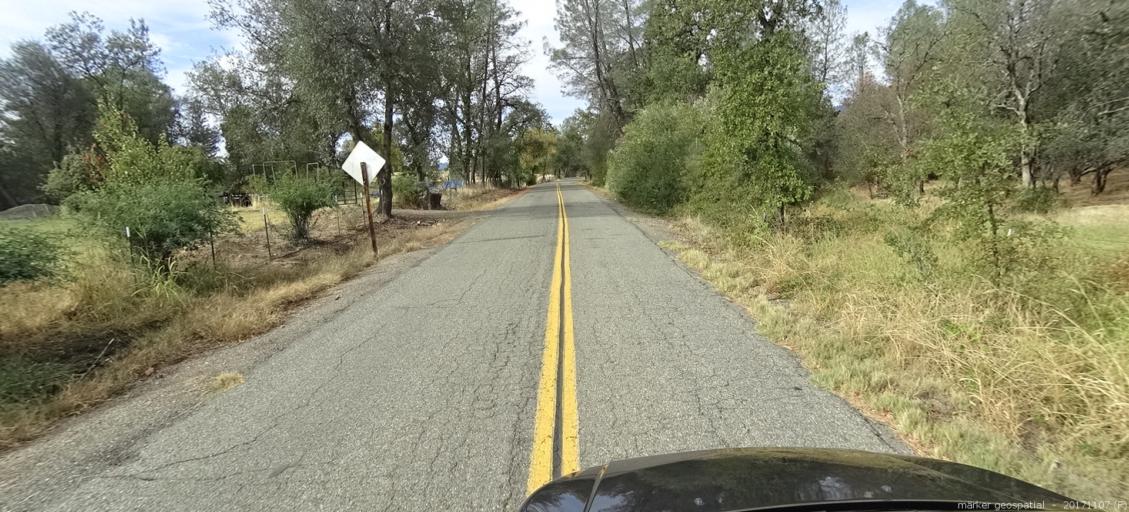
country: US
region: California
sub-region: Shasta County
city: Shasta
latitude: 40.5012
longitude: -122.5697
